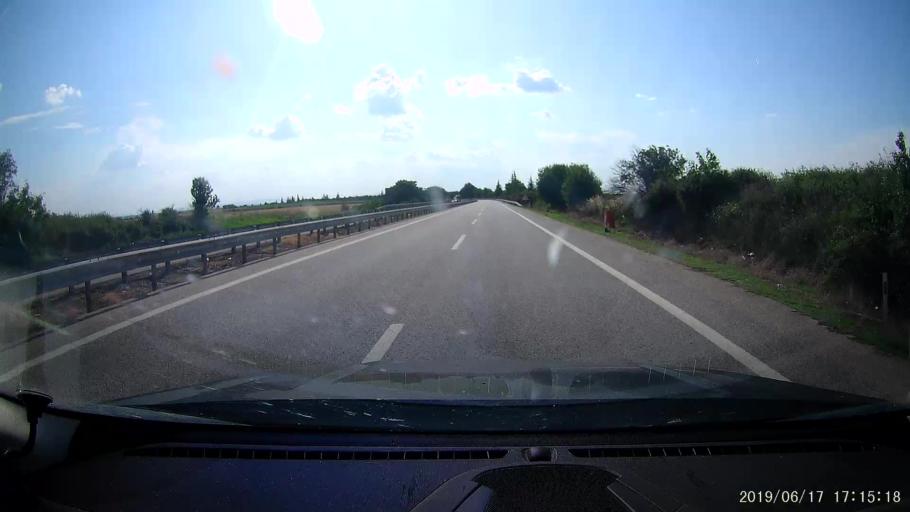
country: GR
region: East Macedonia and Thrace
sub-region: Nomos Evrou
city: Kastanies
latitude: 41.7016
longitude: 26.4993
